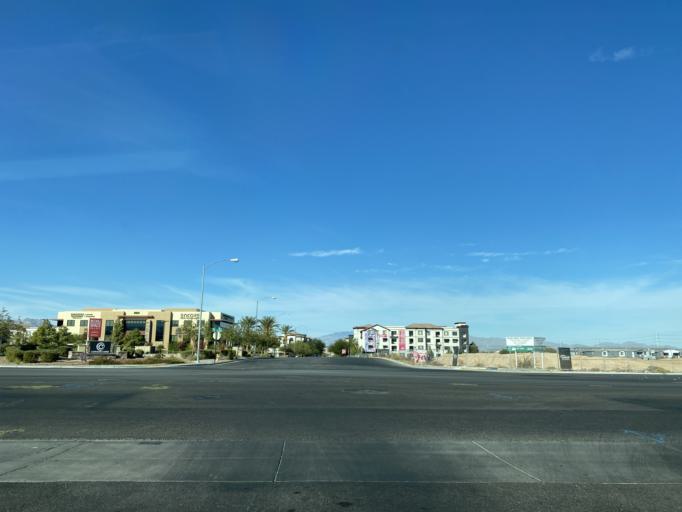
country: US
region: Nevada
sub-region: Clark County
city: Spring Valley
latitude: 36.0701
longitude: -115.2839
